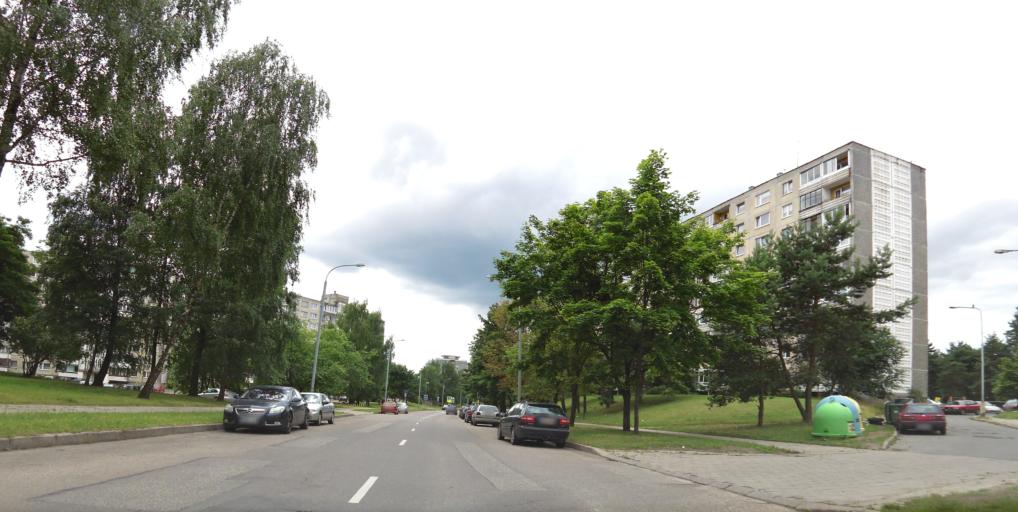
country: LT
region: Vilnius County
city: Justiniskes
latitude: 54.7119
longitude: 25.2237
